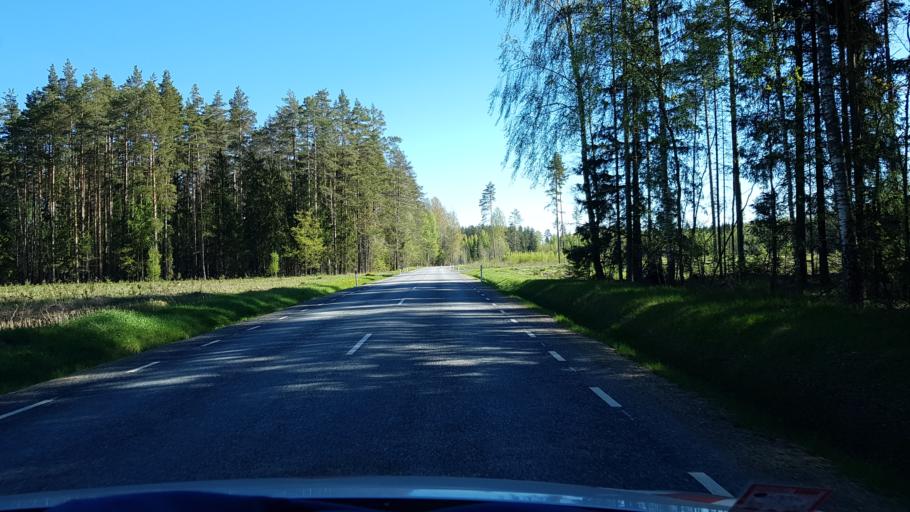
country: EE
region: Polvamaa
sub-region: Polva linn
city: Polva
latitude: 58.1070
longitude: 27.1090
